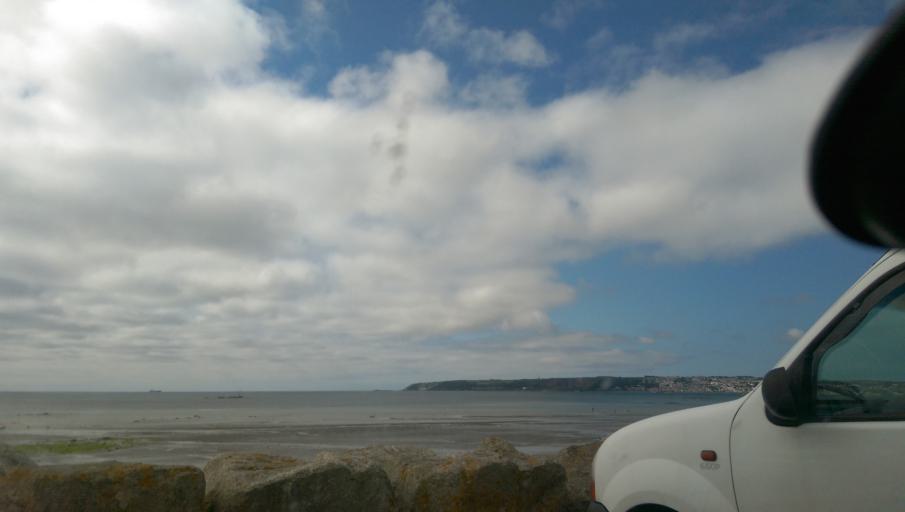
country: GB
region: England
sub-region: Cornwall
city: Marazion
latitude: 50.1281
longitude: -5.5034
